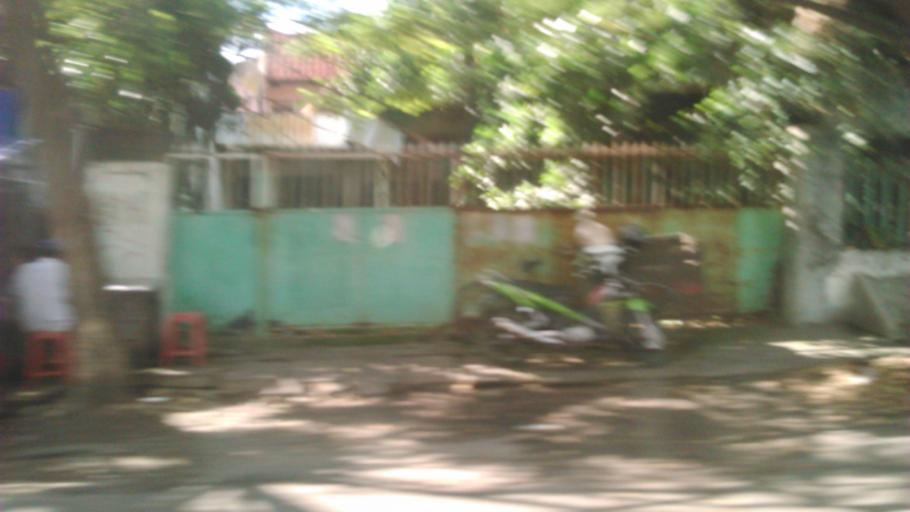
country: ID
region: East Java
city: Pacarkeling
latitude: -7.2574
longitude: 112.7541
